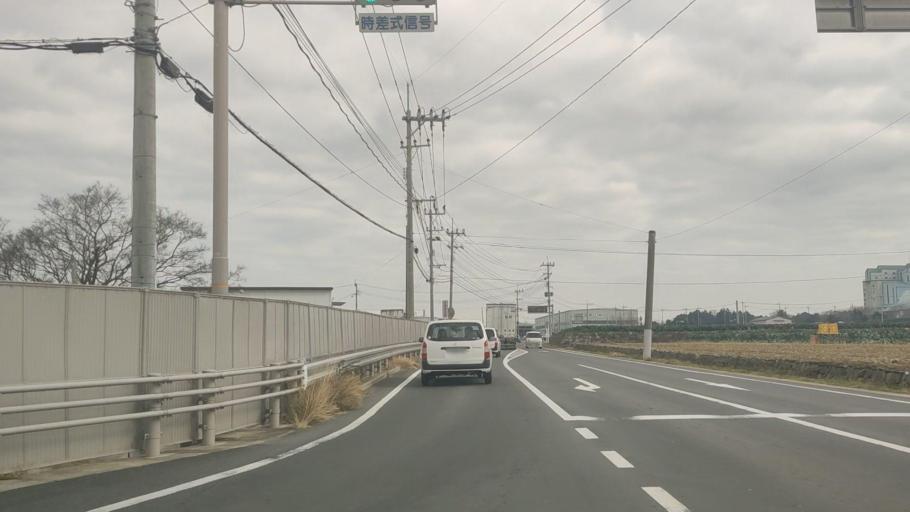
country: JP
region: Nagasaki
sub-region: Isahaya-shi
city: Isahaya
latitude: 32.8177
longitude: 130.1763
